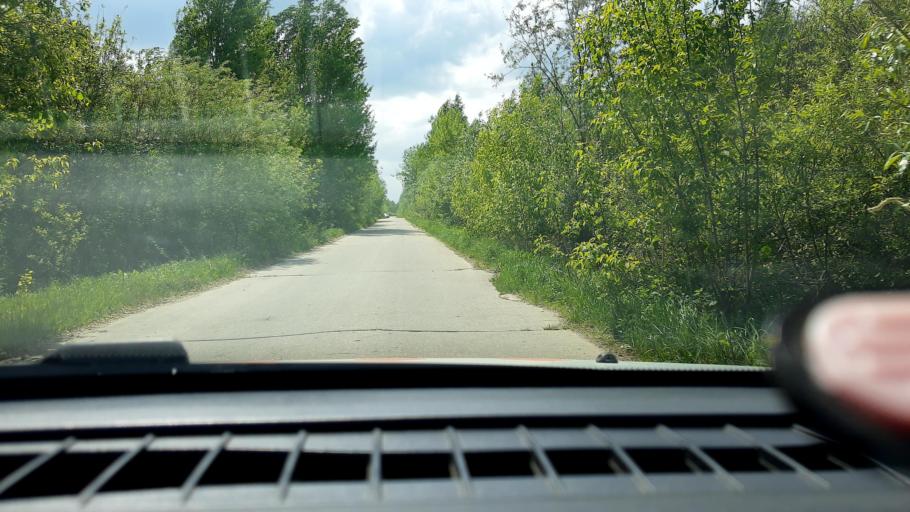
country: RU
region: Nizjnij Novgorod
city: Kstovo
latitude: 56.1404
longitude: 44.1321
